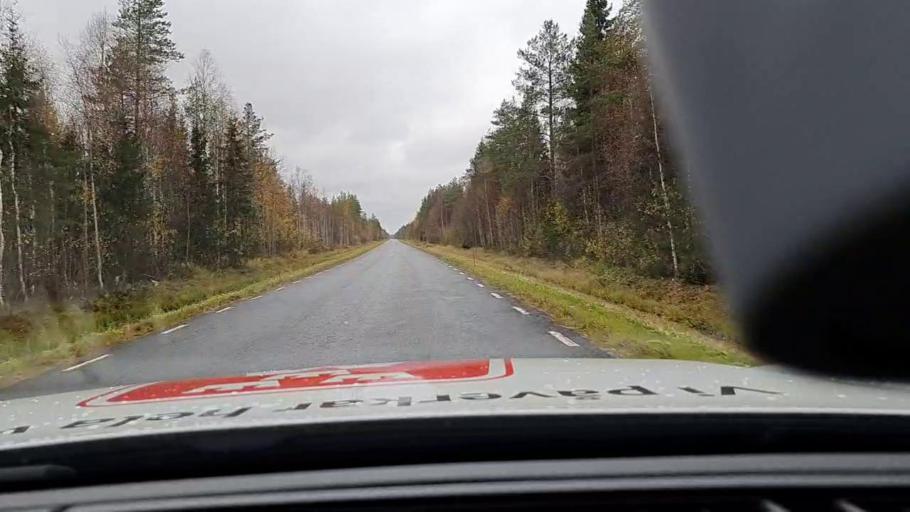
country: SE
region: Norrbotten
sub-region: Haparanda Kommun
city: Haparanda
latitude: 65.9050
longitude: 23.8331
